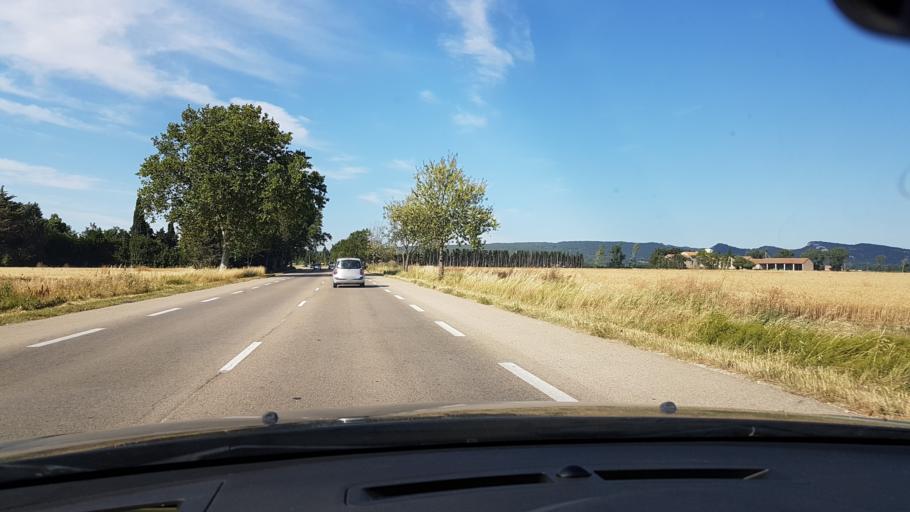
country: FR
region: Provence-Alpes-Cote d'Azur
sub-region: Departement des Bouches-du-Rhone
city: Fontvieille
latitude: 43.7326
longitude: 4.6659
